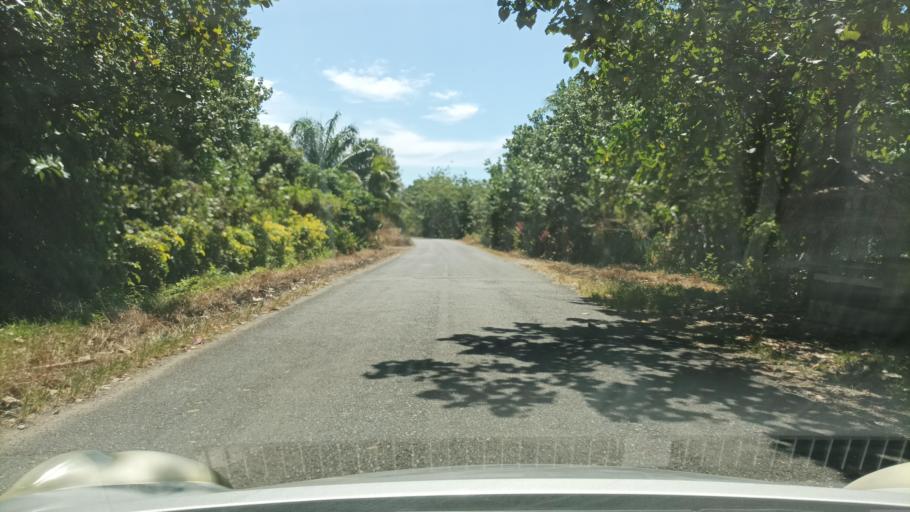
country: SB
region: Guadalcanal
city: Honiara
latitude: -9.3583
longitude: 159.8489
